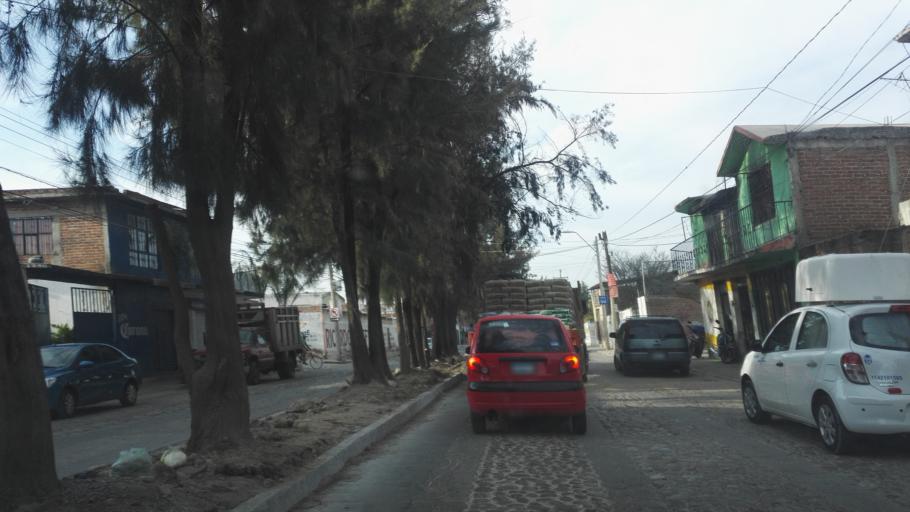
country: MX
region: Guanajuato
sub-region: Leon
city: Fraccionamiento Paraiso Real
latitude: 21.0957
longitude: -101.6050
